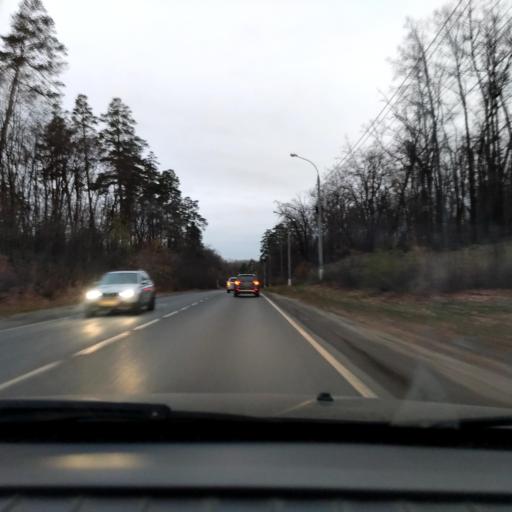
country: RU
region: Samara
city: Tol'yatti
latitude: 53.4923
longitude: 49.2996
